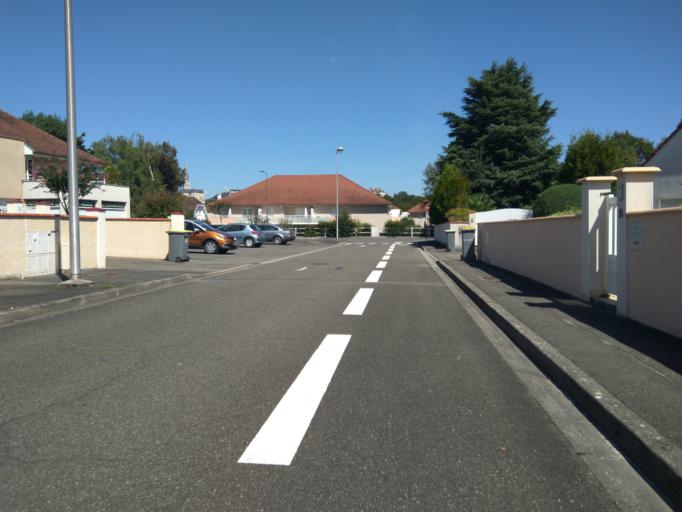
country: FR
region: Aquitaine
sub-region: Departement des Pyrenees-Atlantiques
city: Gelos
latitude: 43.2867
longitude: -0.3752
